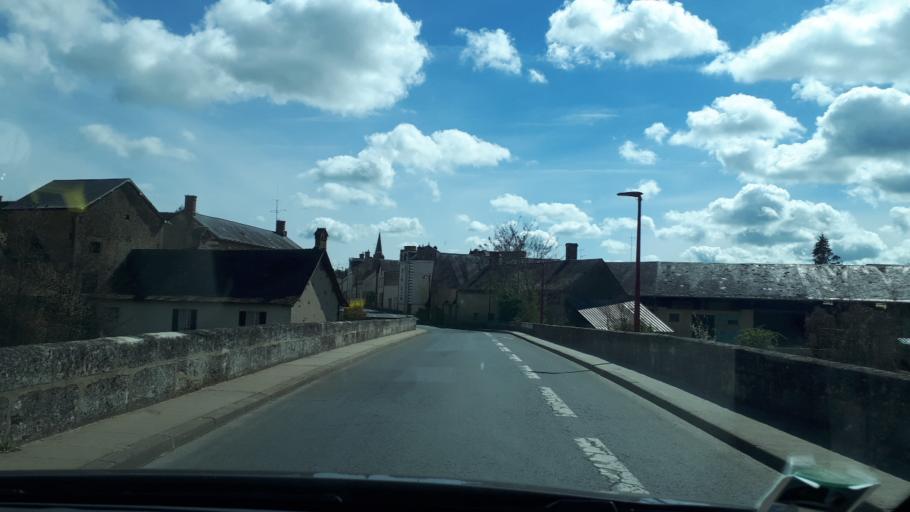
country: FR
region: Centre
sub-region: Departement du Loir-et-Cher
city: Savigny-sur-Braye
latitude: 47.8802
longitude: 0.8035
